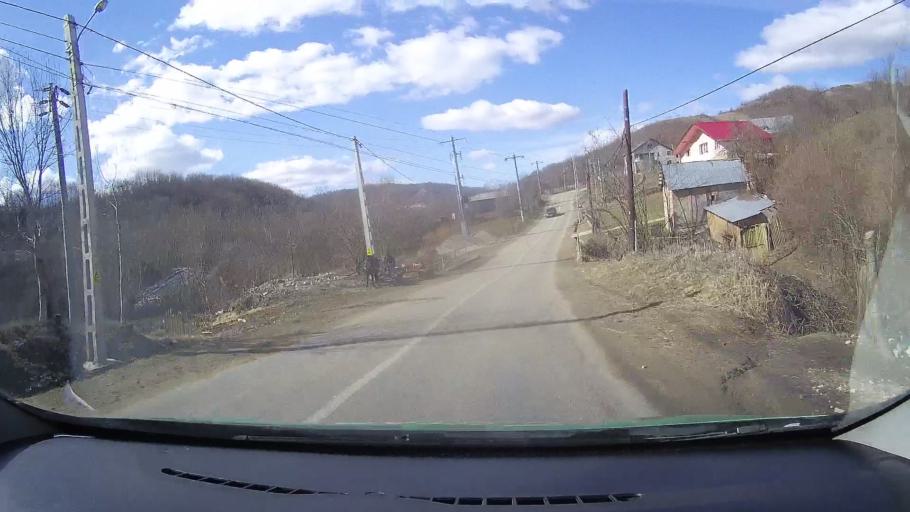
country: RO
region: Dambovita
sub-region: Comuna Glodeni
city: Laculete
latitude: 45.0205
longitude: 25.4469
